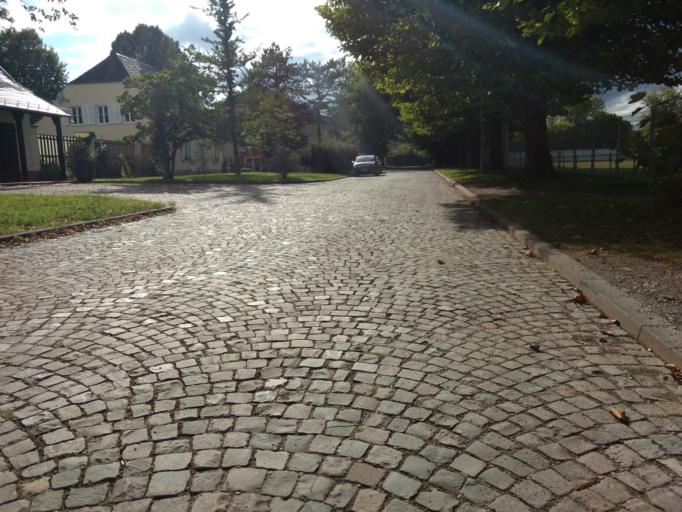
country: DE
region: Saarland
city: Lebach
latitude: 49.4034
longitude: 6.8951
